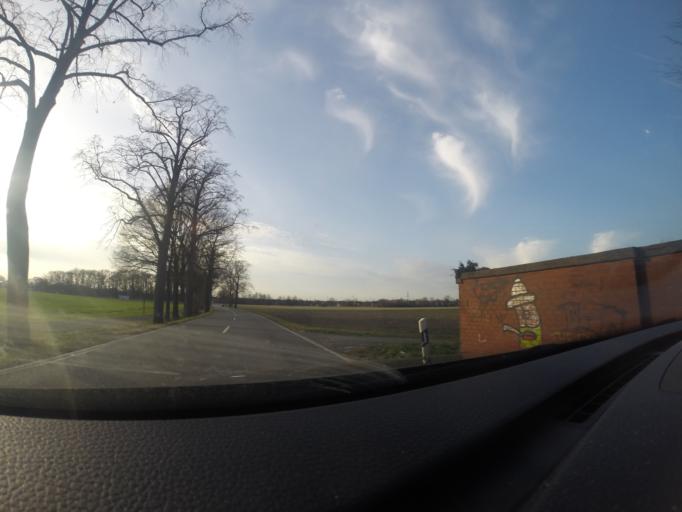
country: DE
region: North Rhine-Westphalia
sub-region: Regierungsbezirk Munster
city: Ahaus
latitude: 52.0885
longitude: 6.9916
